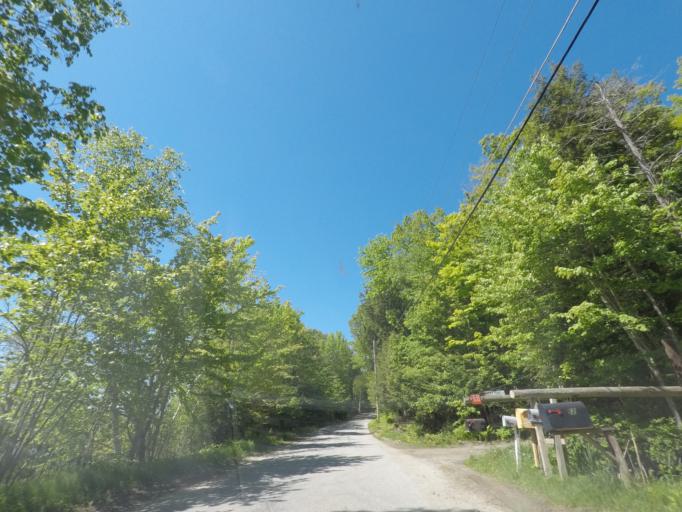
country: US
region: Maine
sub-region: Kennebec County
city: Winthrop
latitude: 44.2645
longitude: -69.9223
